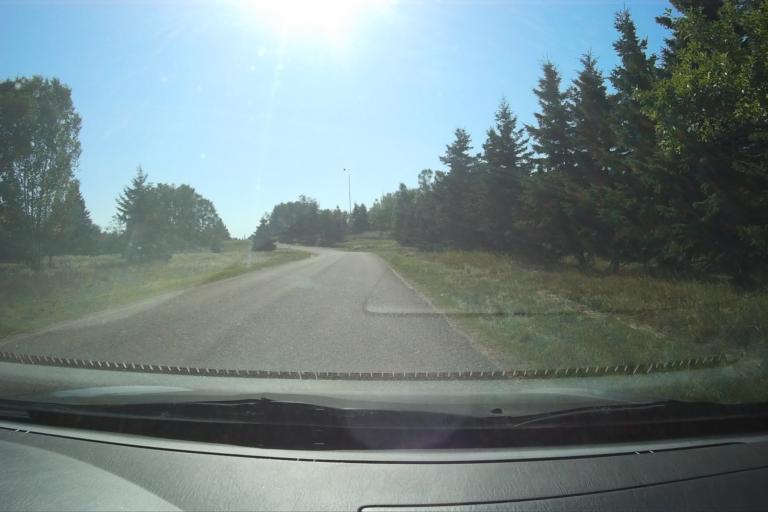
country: CA
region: Ontario
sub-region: Thunder Bay District
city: Thunder Bay
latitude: 48.3326
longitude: -88.8233
